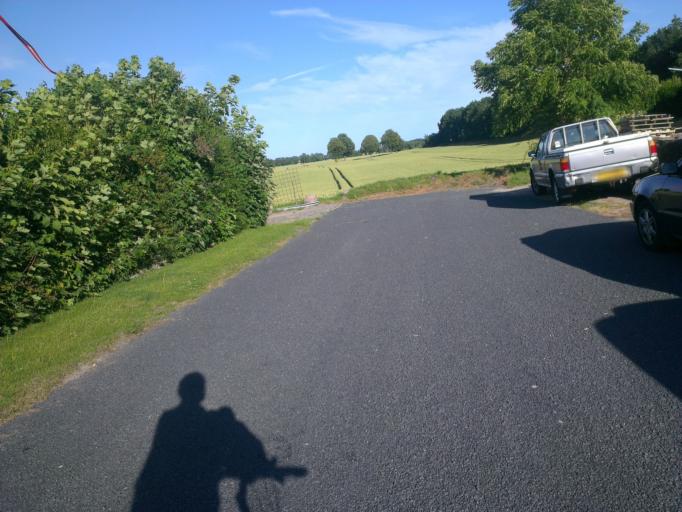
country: DK
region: Capital Region
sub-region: Frederikssund Kommune
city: Skibby
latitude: 55.7926
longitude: 11.9562
